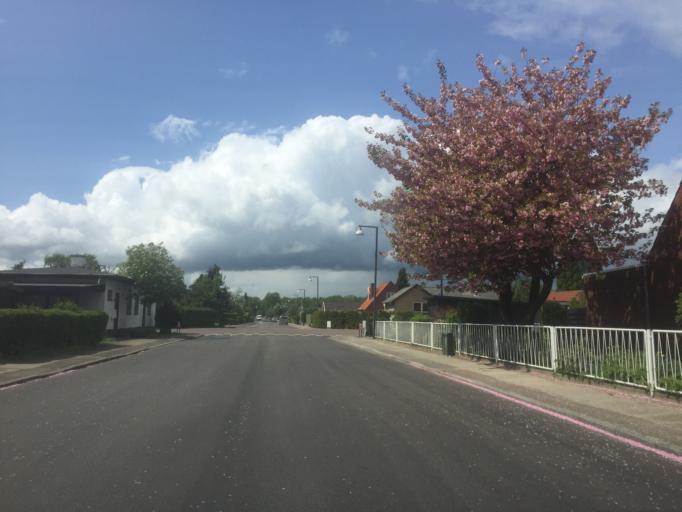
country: DK
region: Capital Region
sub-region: Rodovre Kommune
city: Rodovre
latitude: 55.6857
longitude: 12.4448
